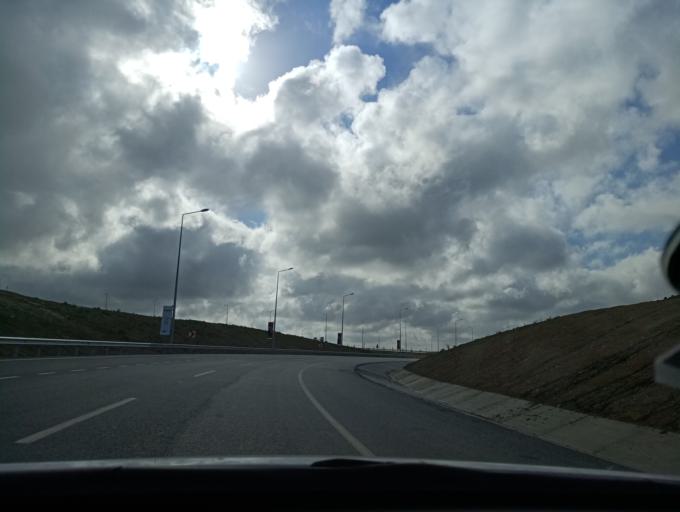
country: TR
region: Istanbul
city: Durusu
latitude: 41.2450
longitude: 28.7383
